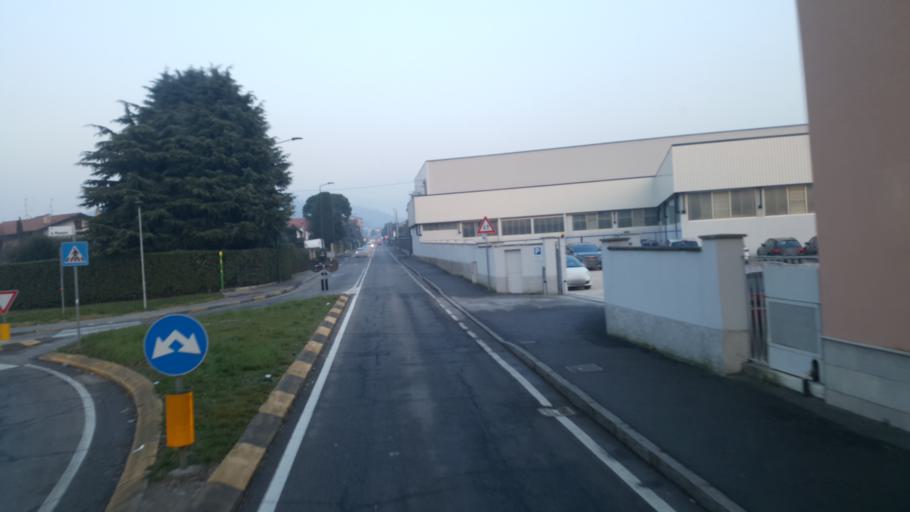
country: IT
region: Lombardy
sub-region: Provincia di Bergamo
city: Scanzo-Rosciate
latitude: 45.7062
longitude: 9.7268
